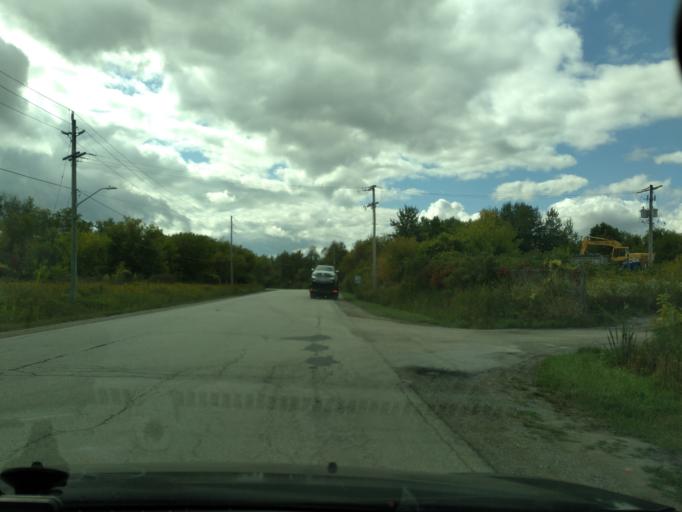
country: CA
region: Ontario
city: Bradford West Gwillimbury
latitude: 44.1316
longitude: -79.5559
